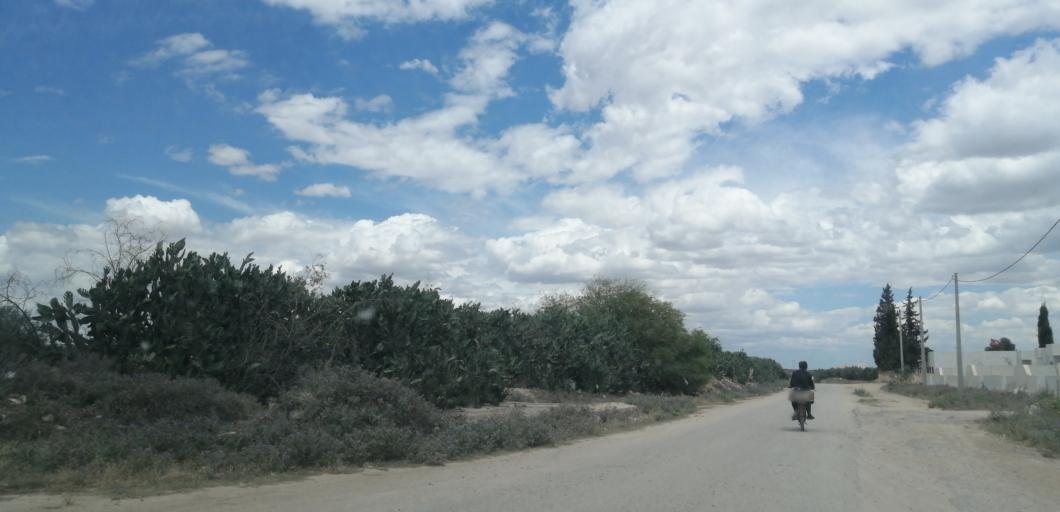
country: TN
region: Al Qayrawan
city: Kairouan
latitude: 35.6233
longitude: 9.9227
